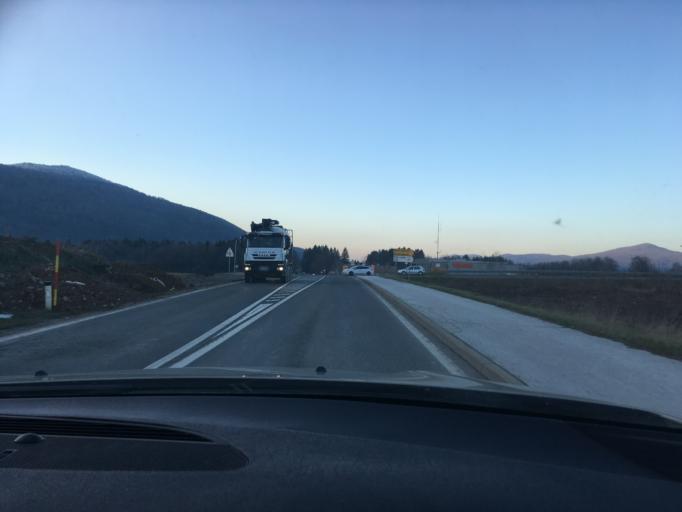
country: SI
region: Kocevje
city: Kocevje
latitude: 45.6522
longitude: 14.8525
